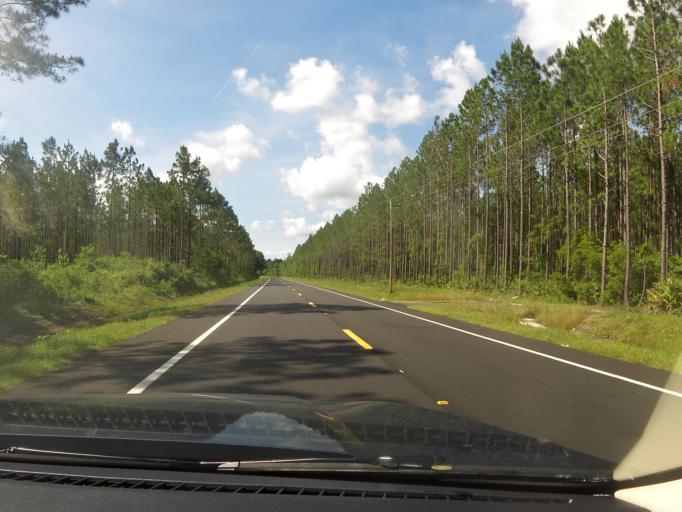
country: US
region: Florida
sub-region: Nassau County
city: Hilliard
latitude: 30.6605
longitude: -81.9034
